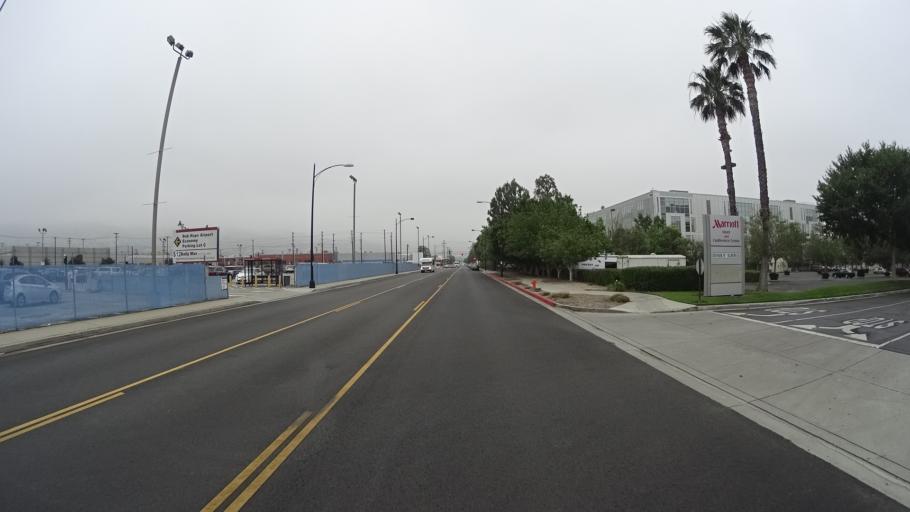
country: US
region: California
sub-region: Los Angeles County
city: North Hollywood
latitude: 34.1956
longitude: -118.3464
